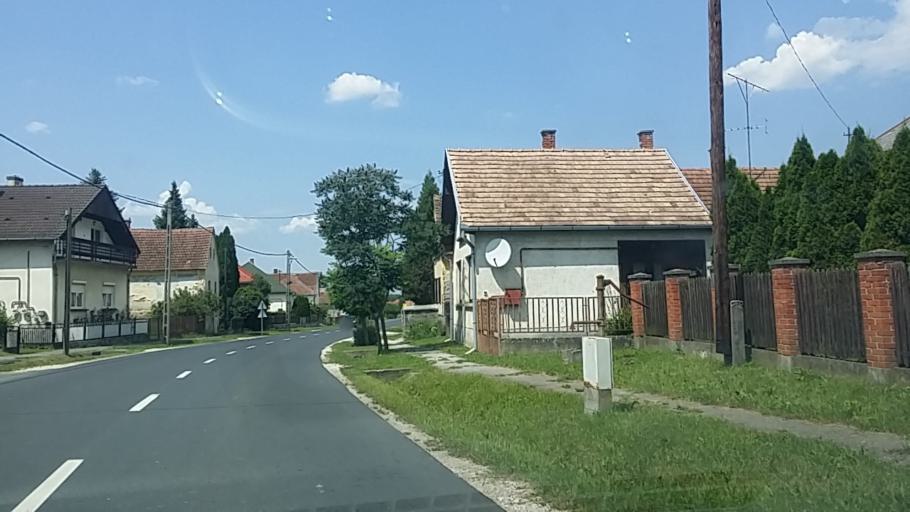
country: HR
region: Medimurska
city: Podturen
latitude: 46.5218
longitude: 16.5553
